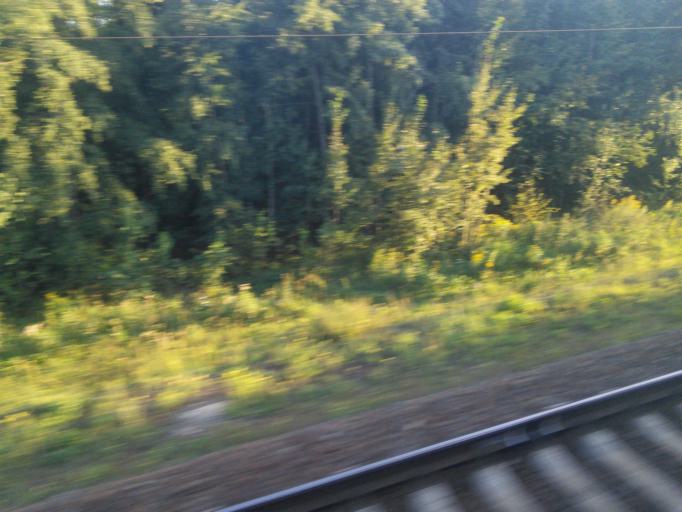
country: RU
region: Moskovskaya
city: Imeni Vorovskogo
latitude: 55.7214
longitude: 38.3327
